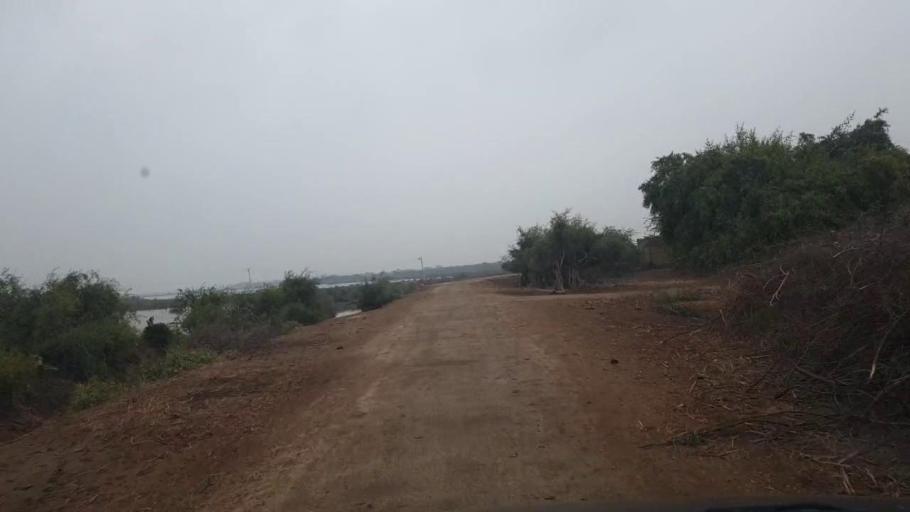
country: PK
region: Sindh
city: Tando Adam
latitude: 25.8311
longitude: 68.6993
